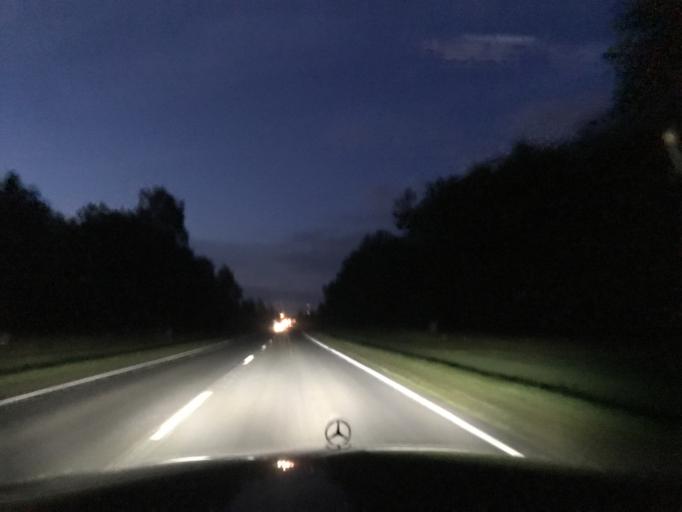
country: BY
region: Brest
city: Brest
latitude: 52.0356
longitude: 23.7289
